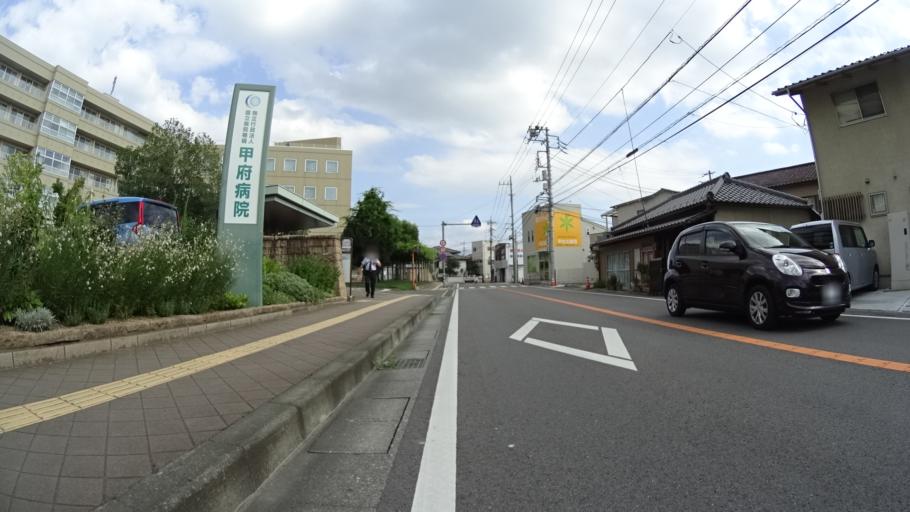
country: JP
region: Yamanashi
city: Kofu-shi
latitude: 35.6771
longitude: 138.5665
